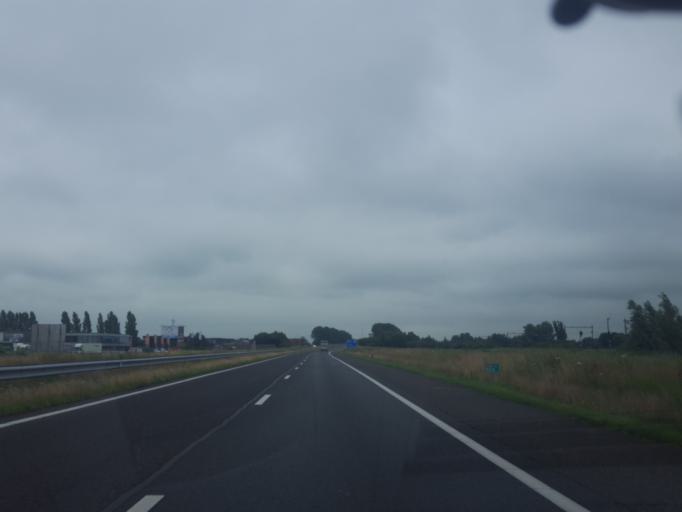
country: NL
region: Friesland
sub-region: Gemeente Boarnsterhim
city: Grou
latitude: 53.0986
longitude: 5.8190
